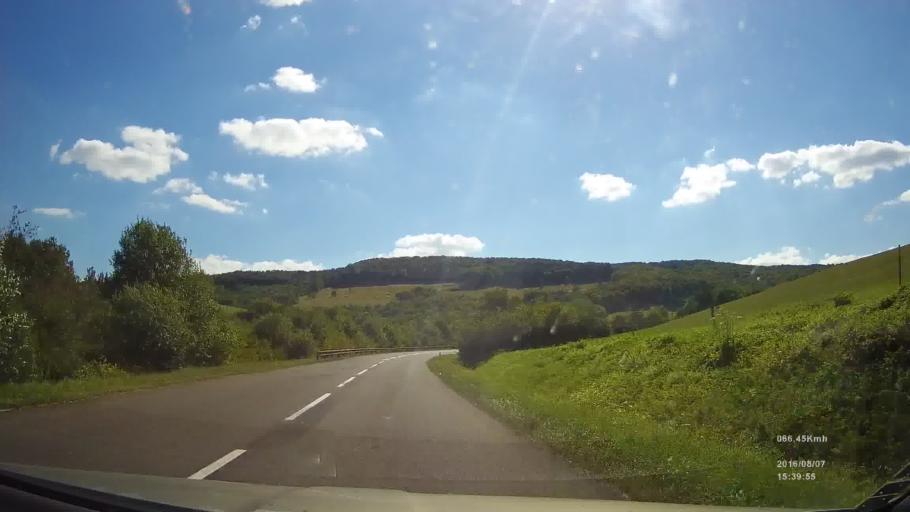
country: SK
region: Presovsky
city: Giraltovce
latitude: 49.1182
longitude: 21.5983
